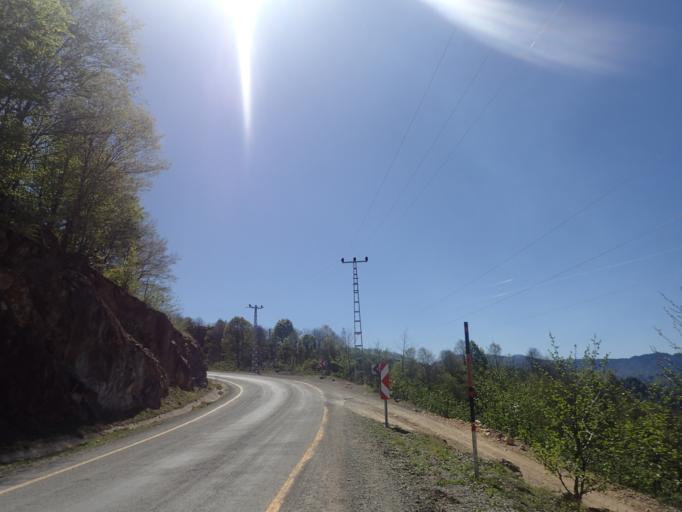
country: TR
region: Ordu
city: Kabaduz
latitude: 40.8005
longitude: 37.9102
